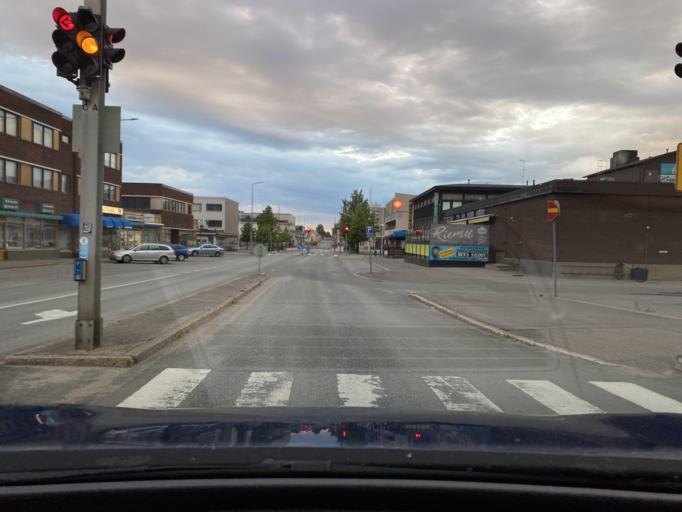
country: FI
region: Northern Ostrobothnia
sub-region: Raahe
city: Raahe
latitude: 64.6834
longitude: 24.4795
